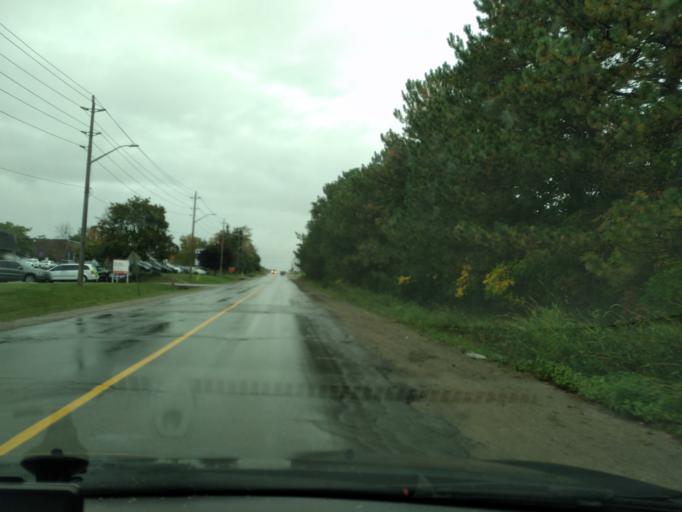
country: CA
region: Ontario
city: Barrie
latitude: 44.4080
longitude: -79.6822
